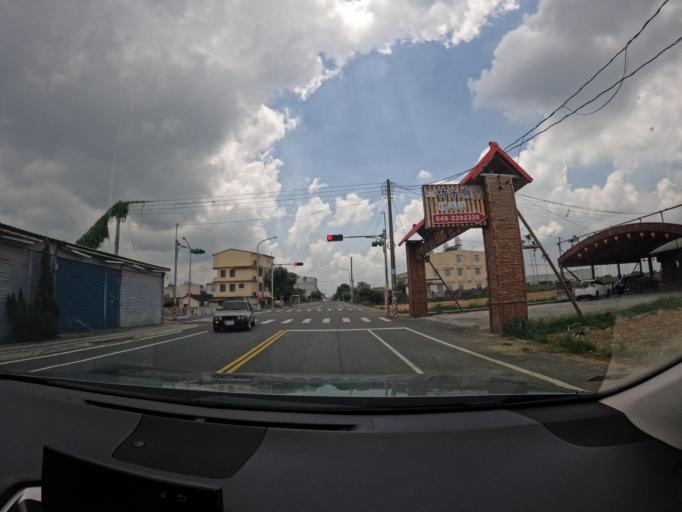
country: TW
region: Taiwan
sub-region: Nantou
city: Nantou
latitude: 23.9123
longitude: 120.6373
